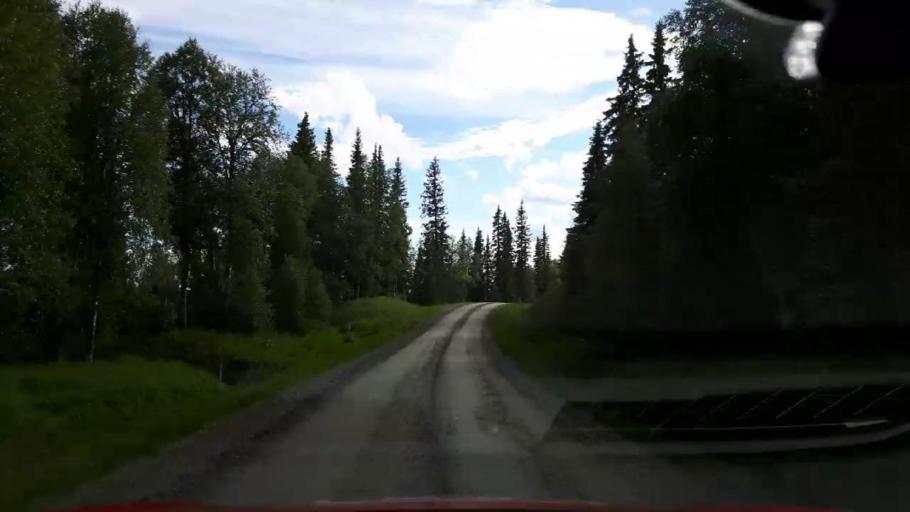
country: SE
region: Jaemtland
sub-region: Krokoms Kommun
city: Valla
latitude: 63.8569
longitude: 14.0964
